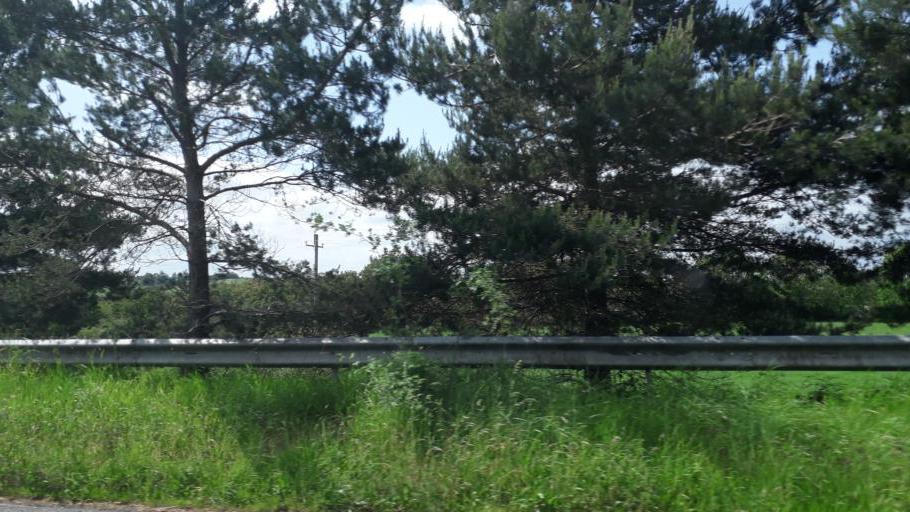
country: IE
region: Leinster
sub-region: Kildare
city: Moone
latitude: 53.0041
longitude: -6.8050
